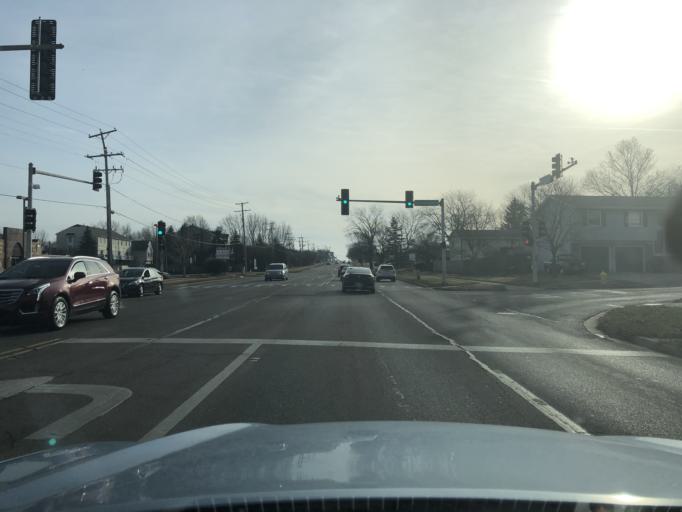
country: US
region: Illinois
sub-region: DuPage County
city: Glendale Heights
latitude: 41.9247
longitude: -88.0811
